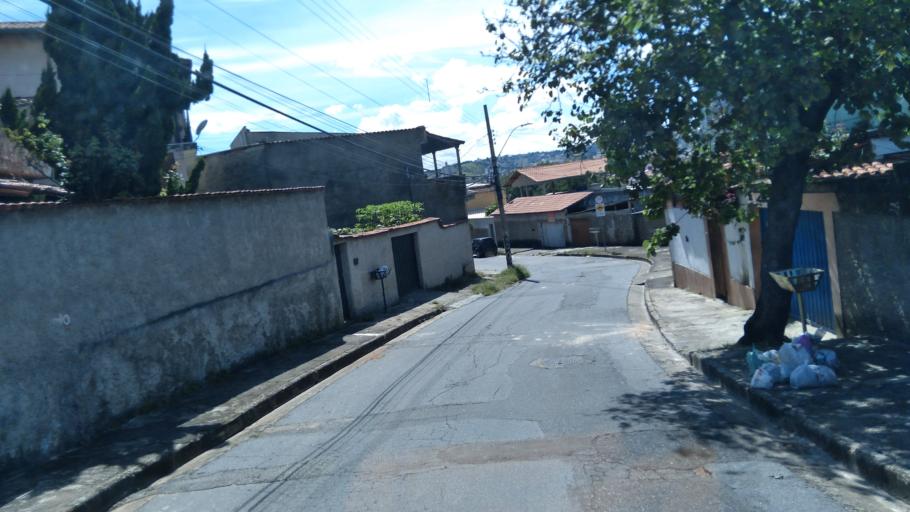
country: BR
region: Minas Gerais
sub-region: Contagem
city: Contagem
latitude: -19.8935
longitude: -44.0131
